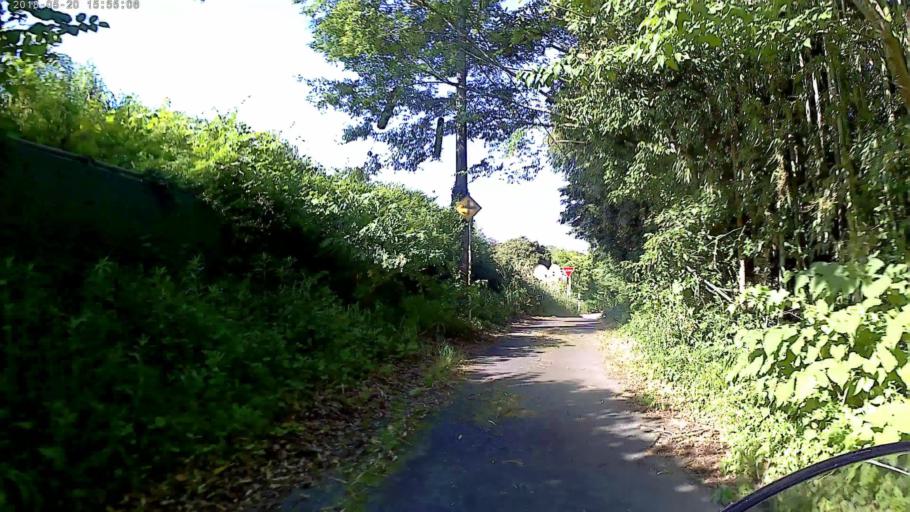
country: JP
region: Kanagawa
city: Hadano
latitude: 35.3295
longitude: 139.2048
